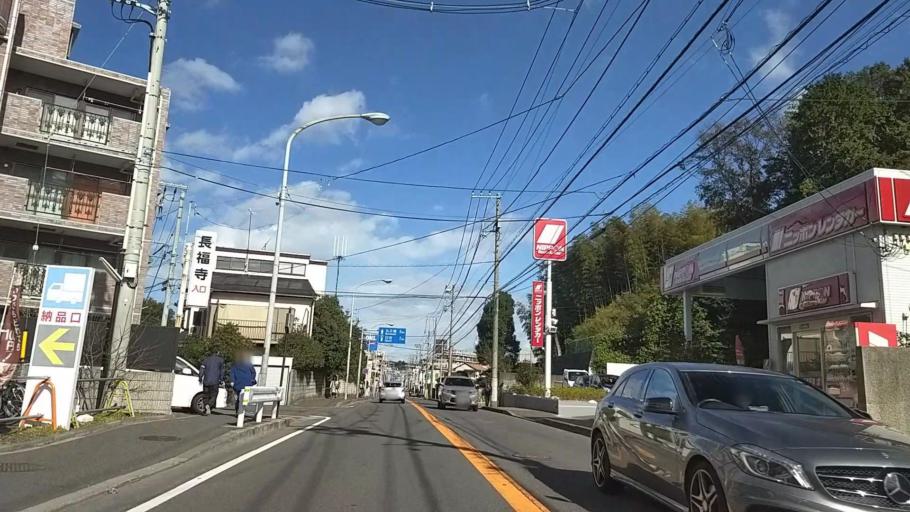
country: JP
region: Kanagawa
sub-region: Kawasaki-shi
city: Kawasaki
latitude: 35.5380
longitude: 139.6369
